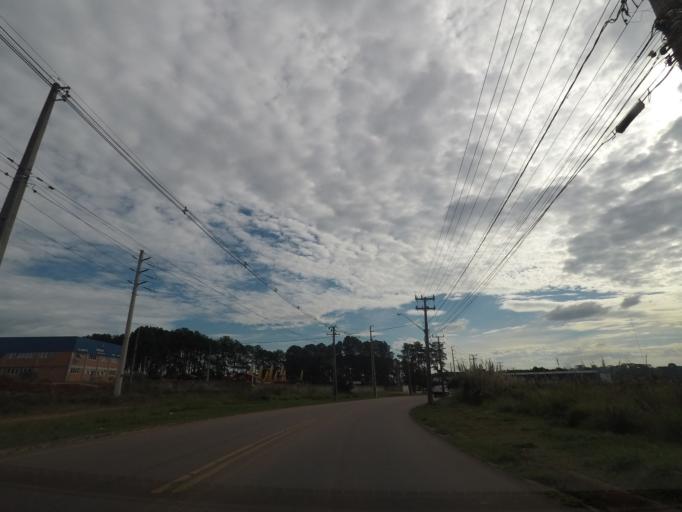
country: BR
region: Parana
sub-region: Sao Jose Dos Pinhais
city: Sao Jose dos Pinhais
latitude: -25.6307
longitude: -49.2858
